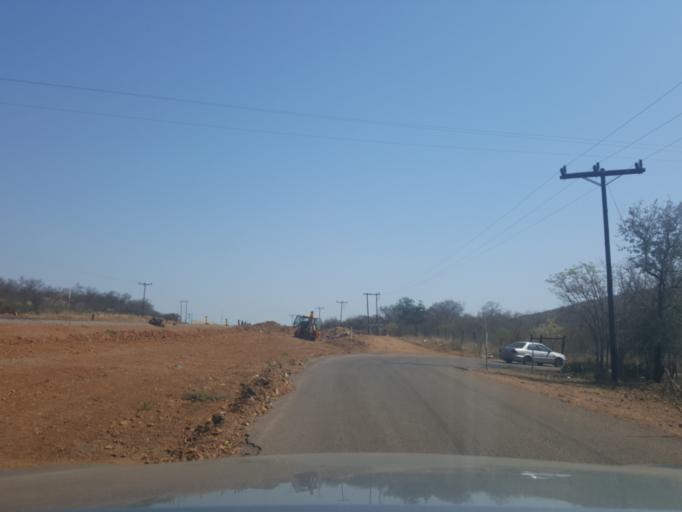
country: BW
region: Kweneng
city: Gabane
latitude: -24.7449
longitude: 25.8307
